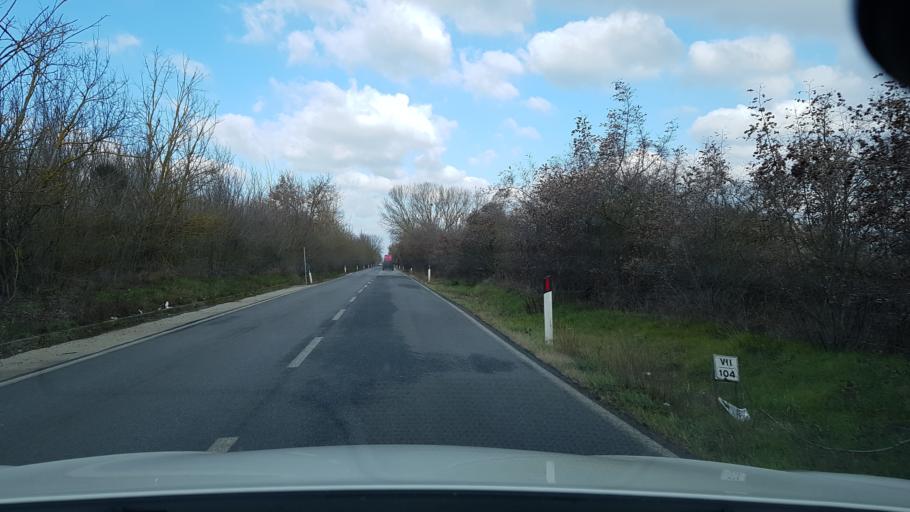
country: IT
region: Umbria
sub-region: Provincia di Perugia
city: Castiglione del Lago
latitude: 43.1354
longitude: 12.0272
